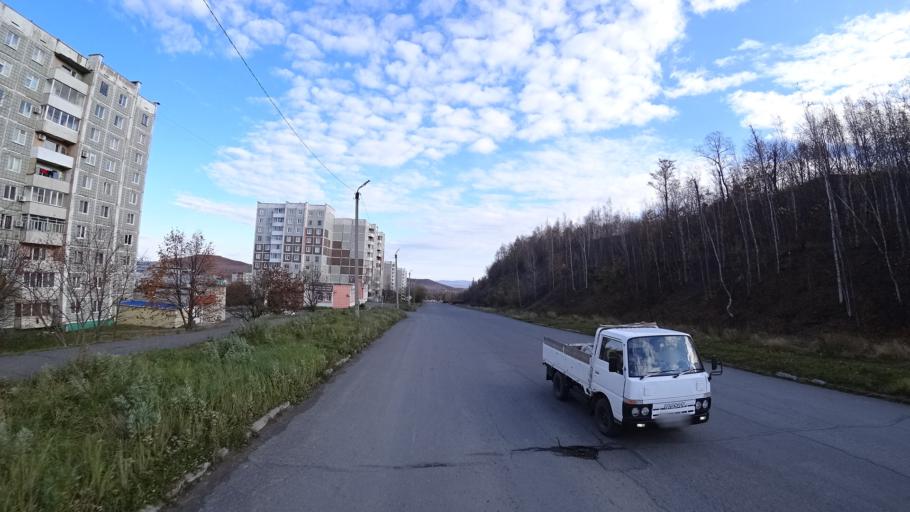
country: RU
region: Khabarovsk Krai
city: Amursk
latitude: 50.2451
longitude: 136.9213
